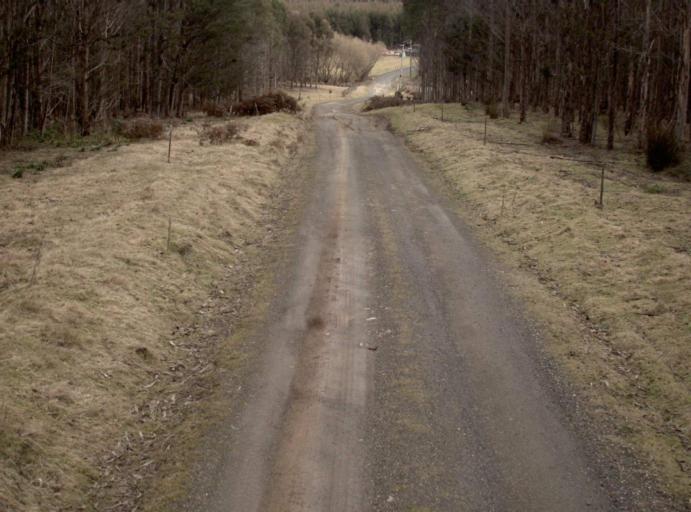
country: AU
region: Tasmania
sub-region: Dorset
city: Scottsdale
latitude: -41.2722
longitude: 147.3488
